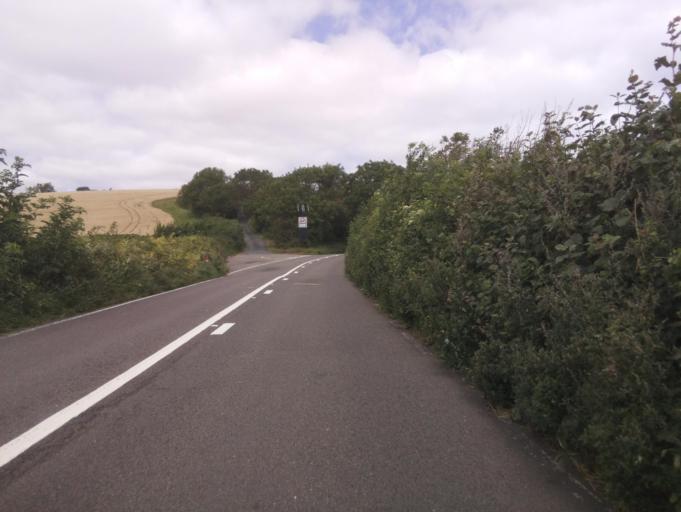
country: GB
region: England
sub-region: Devon
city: Teignmouth
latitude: 50.5261
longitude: -3.5093
